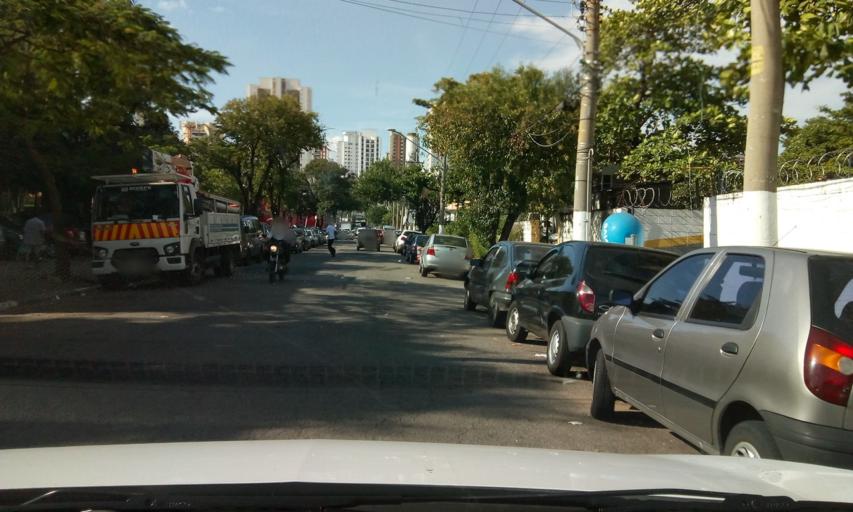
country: BR
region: Sao Paulo
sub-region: Osasco
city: Osasco
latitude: -23.5358
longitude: -46.7317
